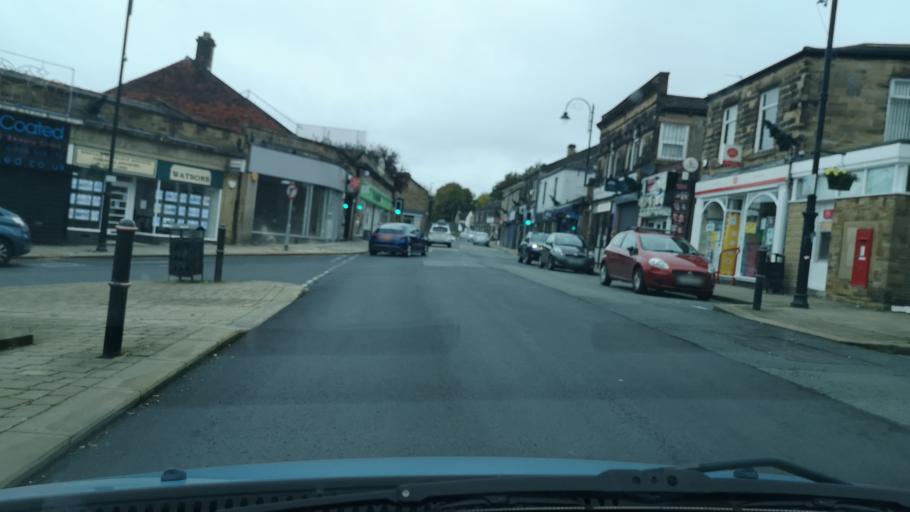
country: GB
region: England
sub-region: City and Borough of Leeds
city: Drighlington
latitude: 53.7321
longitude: -1.6605
